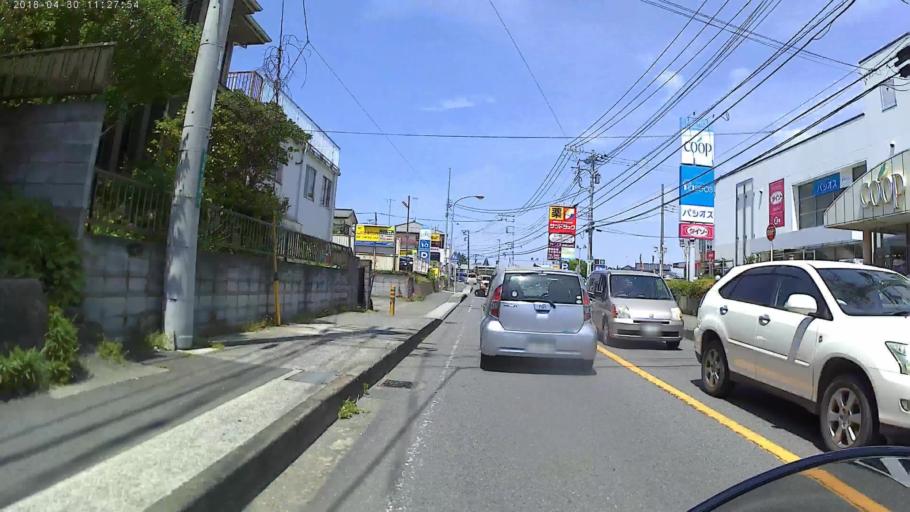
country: JP
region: Kanagawa
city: Zama
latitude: 35.4806
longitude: 139.4116
